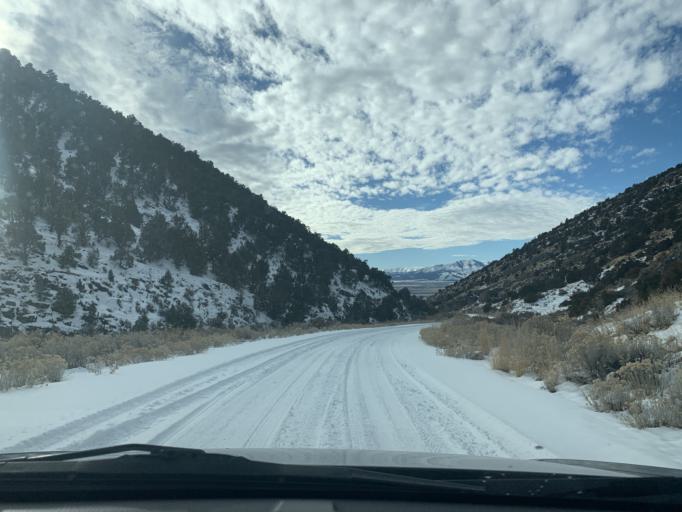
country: US
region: Utah
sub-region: Tooele County
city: Tooele
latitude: 40.3129
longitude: -112.2402
